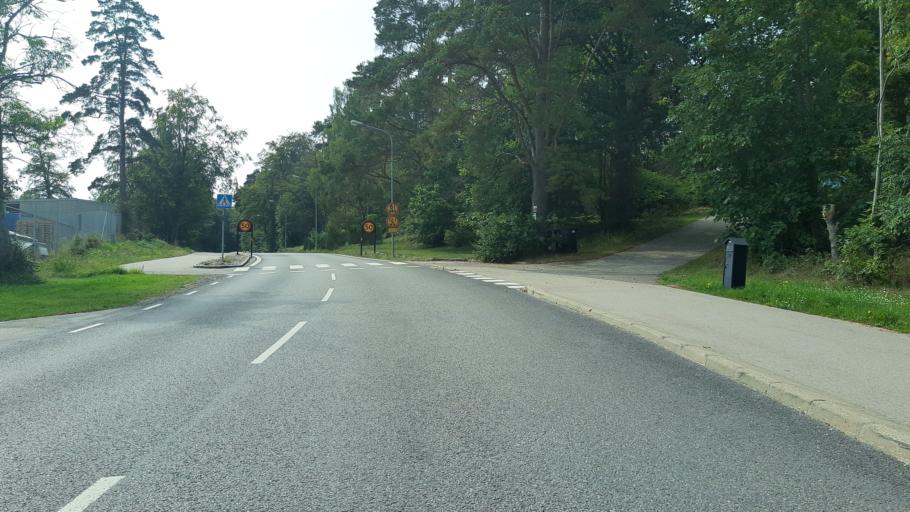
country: SE
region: Blekinge
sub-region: Ronneby Kommun
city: Ronneby
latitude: 56.1758
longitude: 15.2962
